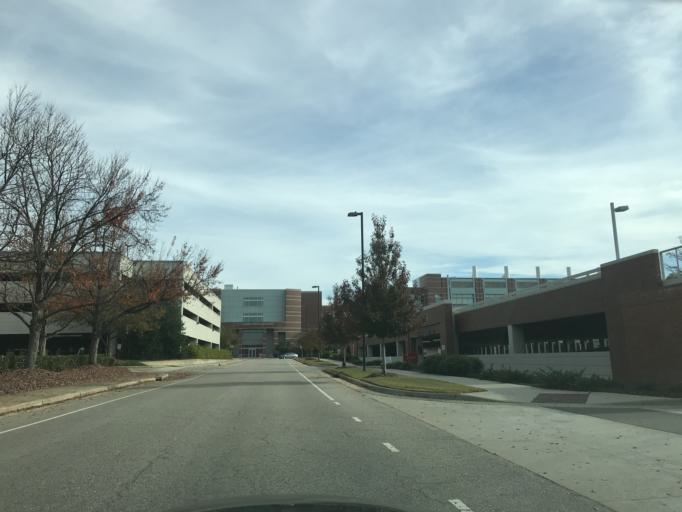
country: US
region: North Carolina
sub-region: Wake County
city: West Raleigh
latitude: 35.7732
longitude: -78.6762
